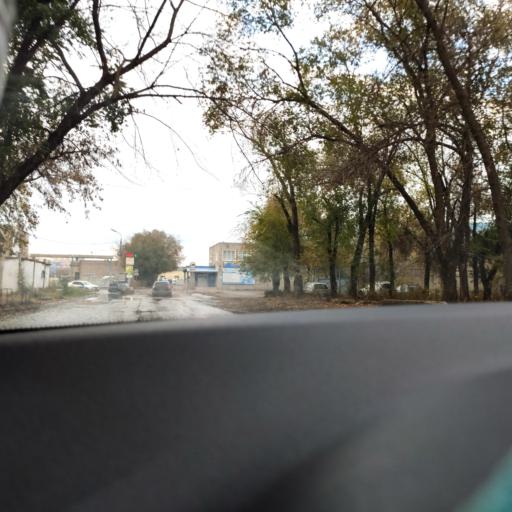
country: RU
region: Samara
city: Samara
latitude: 53.2008
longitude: 50.2546
